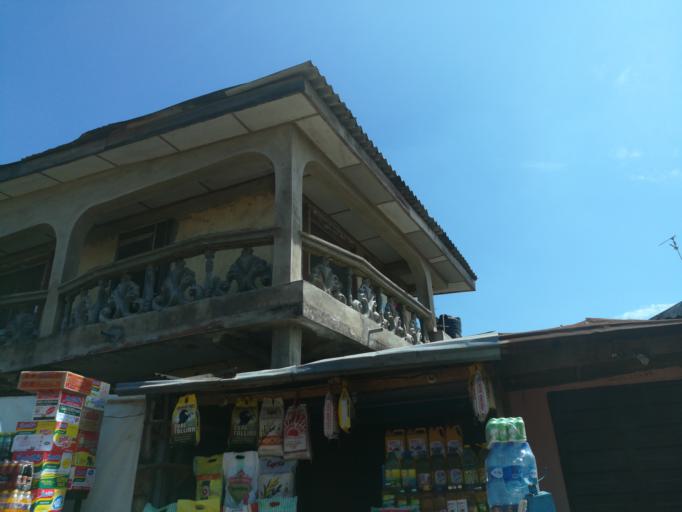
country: NG
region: Lagos
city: Oshodi
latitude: 6.5680
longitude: 3.3346
